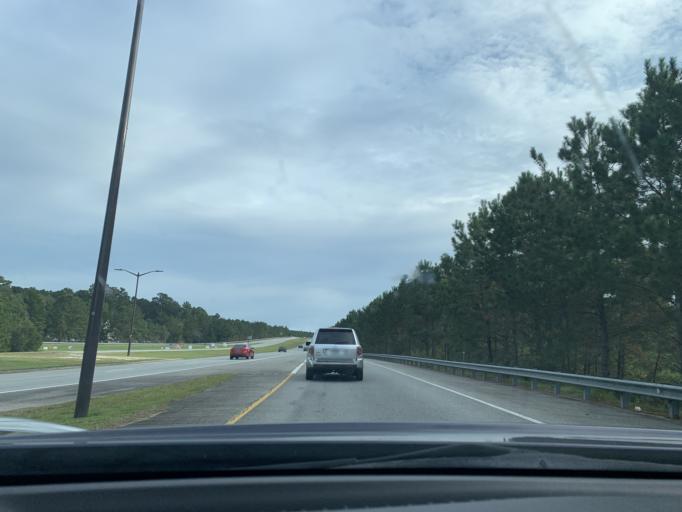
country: US
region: Georgia
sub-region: Chatham County
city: Pooler
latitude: 32.1166
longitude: -81.2693
